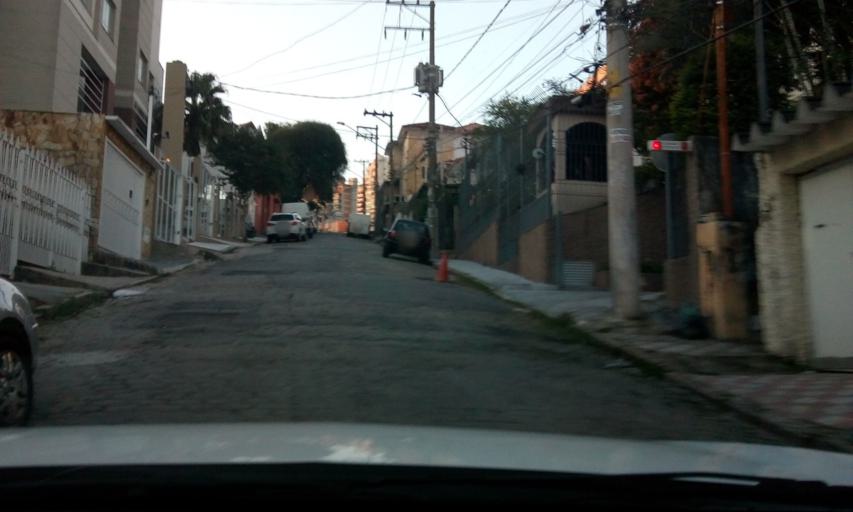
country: BR
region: Sao Paulo
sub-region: Sao Paulo
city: Sao Paulo
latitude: -23.4867
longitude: -46.6161
